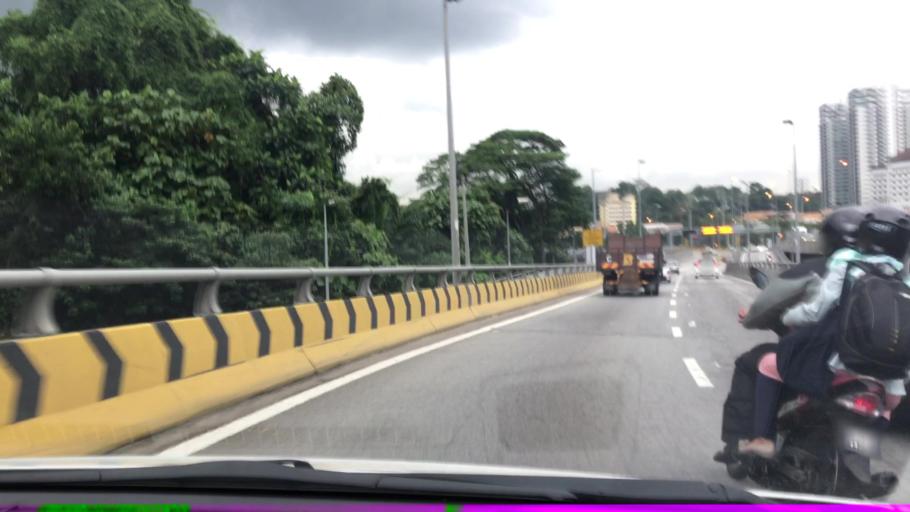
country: MY
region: Kuala Lumpur
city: Kuala Lumpur
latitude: 3.1160
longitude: 101.6619
